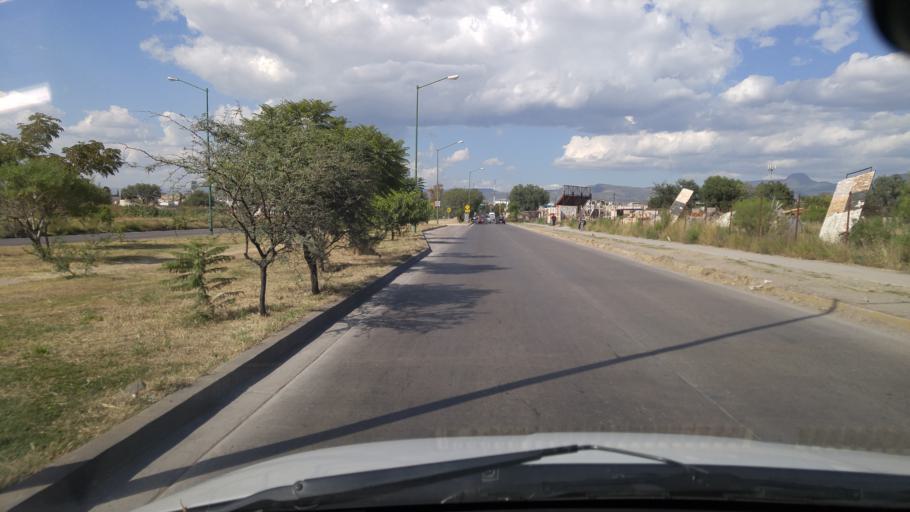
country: MX
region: Guanajuato
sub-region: Leon
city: San Jose de Duran (Los Troncoso)
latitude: 21.0919
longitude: -101.6420
